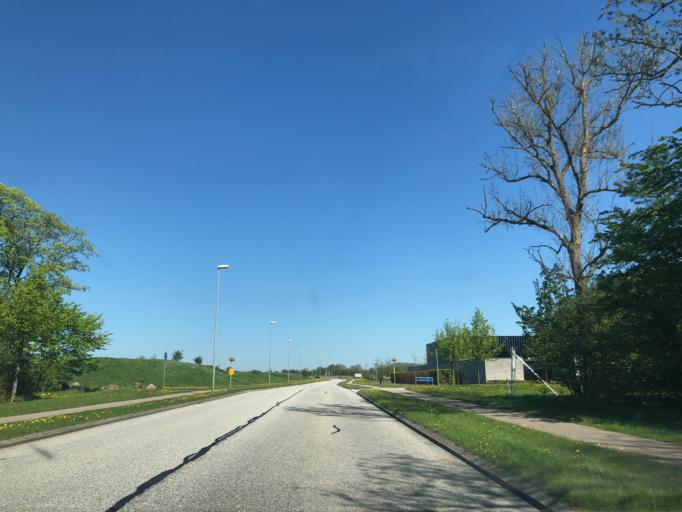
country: DK
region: Zealand
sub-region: Ringsted Kommune
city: Ringsted
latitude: 55.4609
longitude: 11.8196
